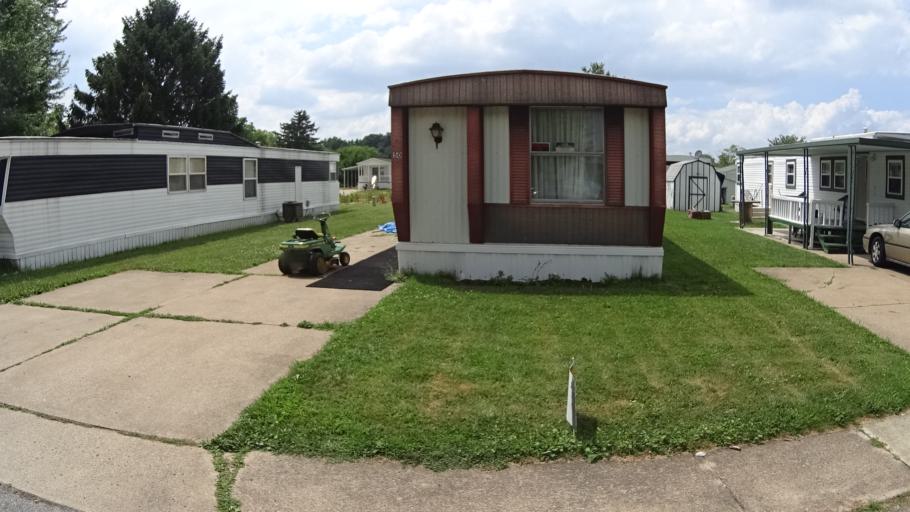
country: US
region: Ohio
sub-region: Erie County
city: Sandusky
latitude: 41.4387
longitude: -82.7574
